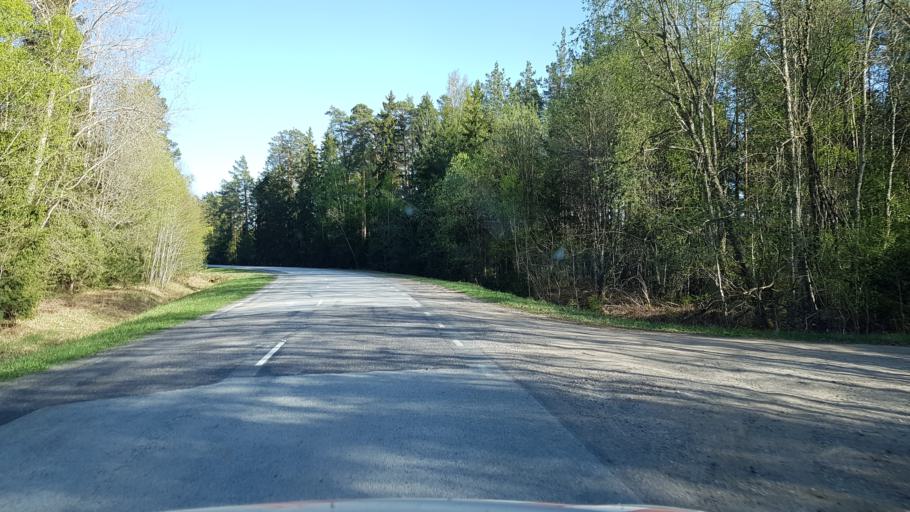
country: EE
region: Paernumaa
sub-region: Paikuse vald
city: Paikuse
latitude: 58.3461
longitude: 24.6700
